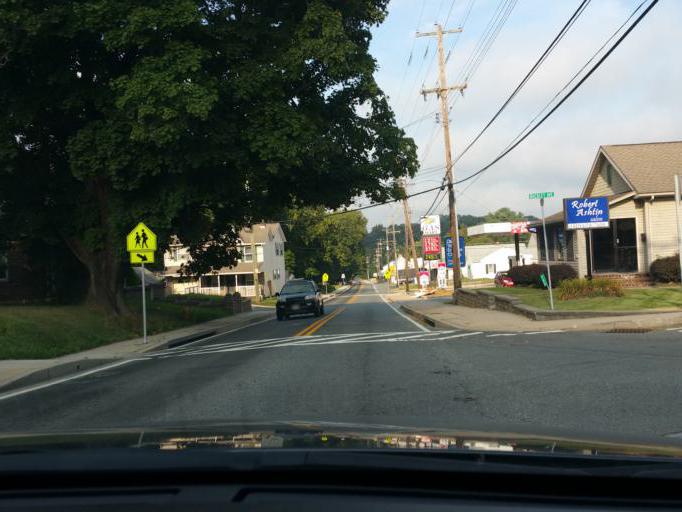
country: US
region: Maryland
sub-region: Cecil County
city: Rising Sun
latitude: 39.6979
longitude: -76.0654
